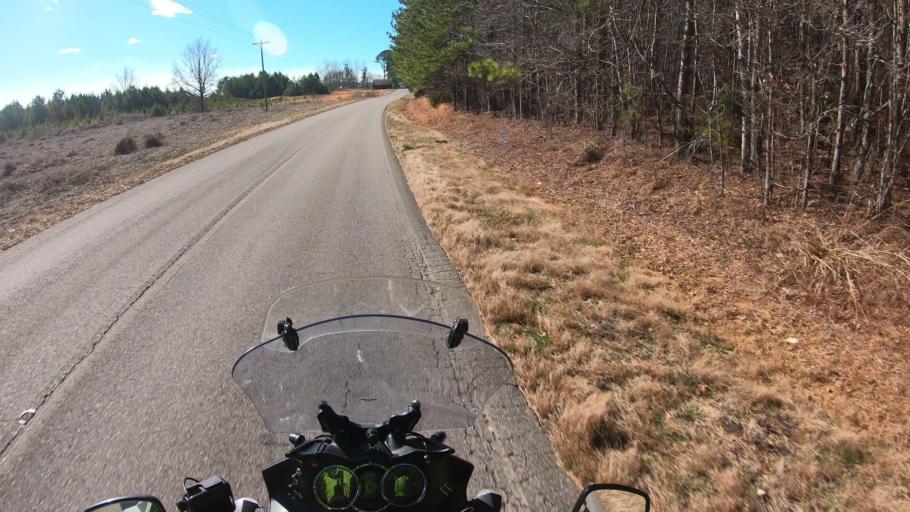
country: US
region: Alabama
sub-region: Clay County
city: Lineville
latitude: 33.4103
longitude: -85.7911
